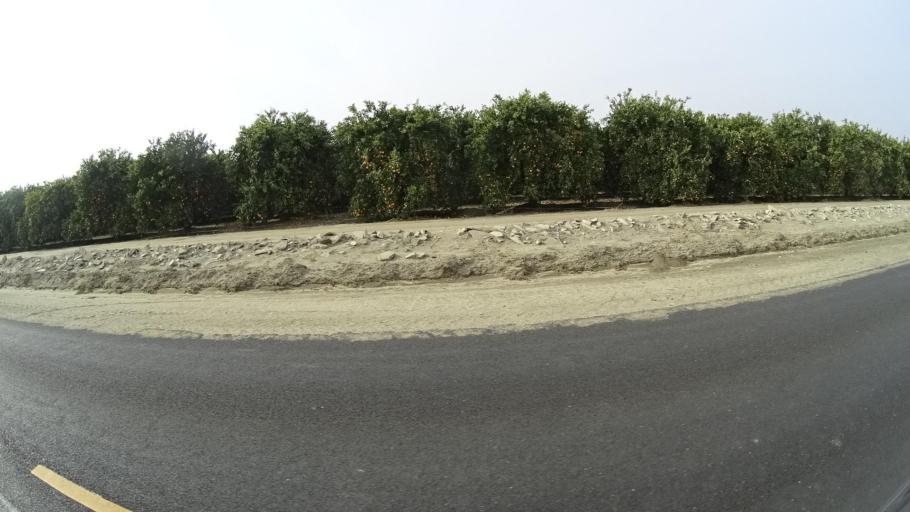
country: US
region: California
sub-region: Kern County
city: Arvin
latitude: 35.1557
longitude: -118.8509
